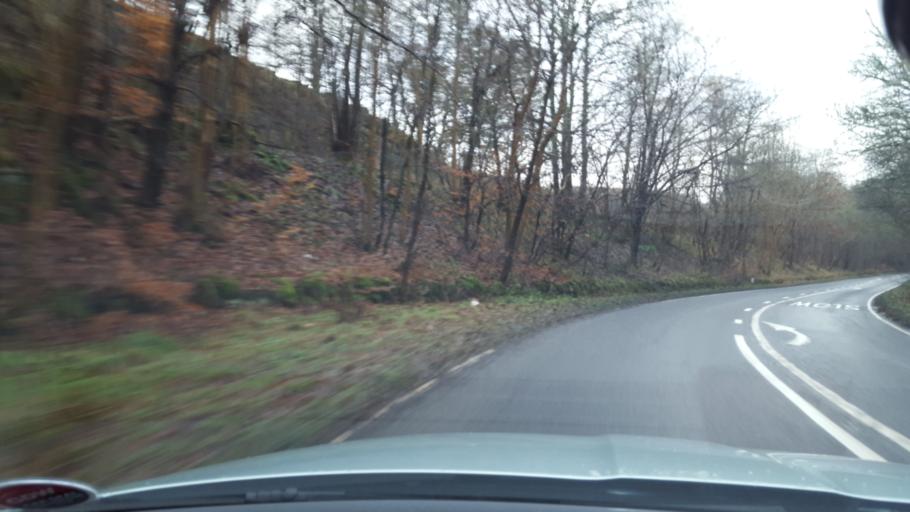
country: GB
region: Scotland
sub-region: Perth and Kinross
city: Bridge of Earn
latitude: 56.3021
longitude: -3.3692
